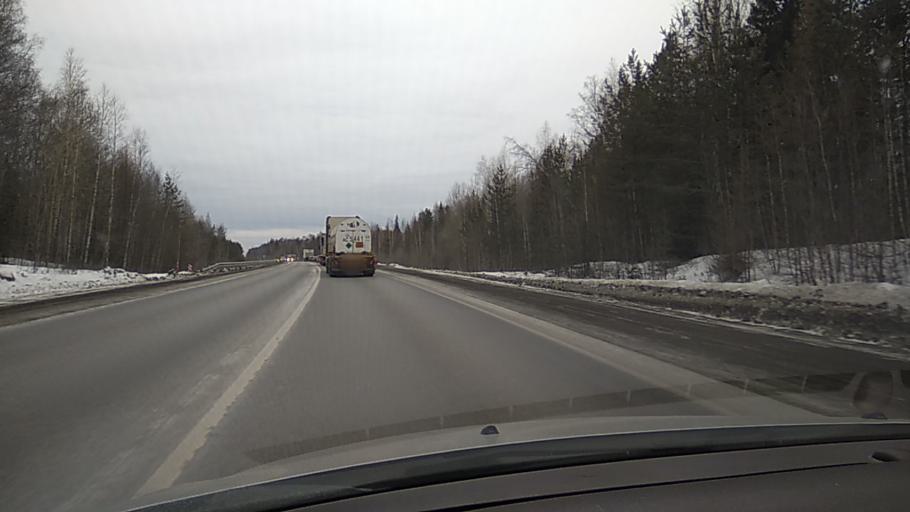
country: RU
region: Sverdlovsk
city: Talitsa
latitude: 56.8387
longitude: 60.0032
